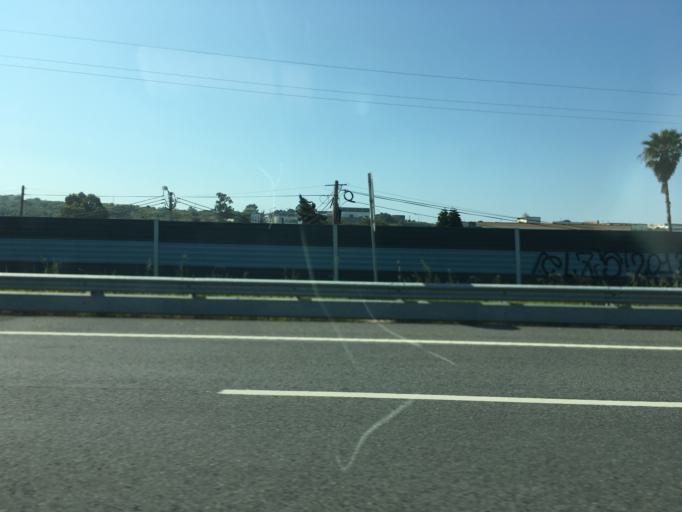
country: PT
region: Lisbon
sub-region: Sintra
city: Pero Pinheiro
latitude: 38.8170
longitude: -9.3370
